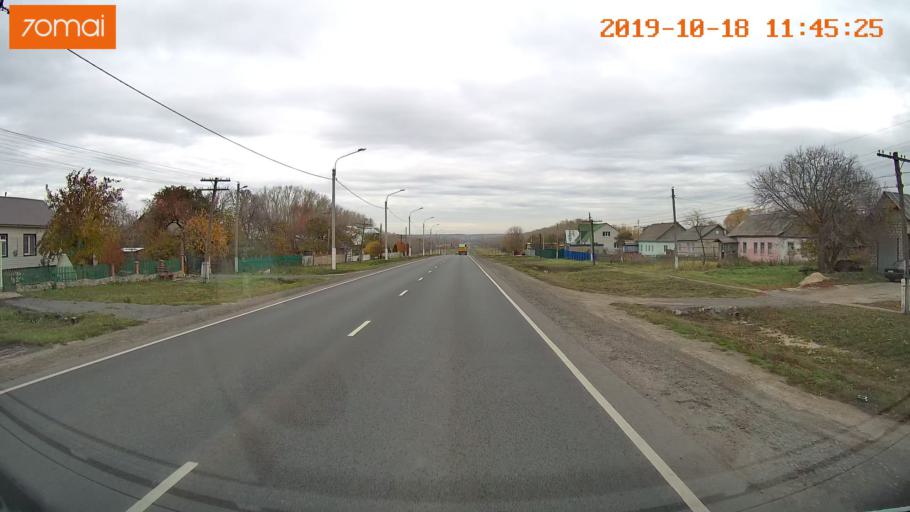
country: RU
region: Rjazan
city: Mikhaylov
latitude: 54.2104
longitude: 38.9699
